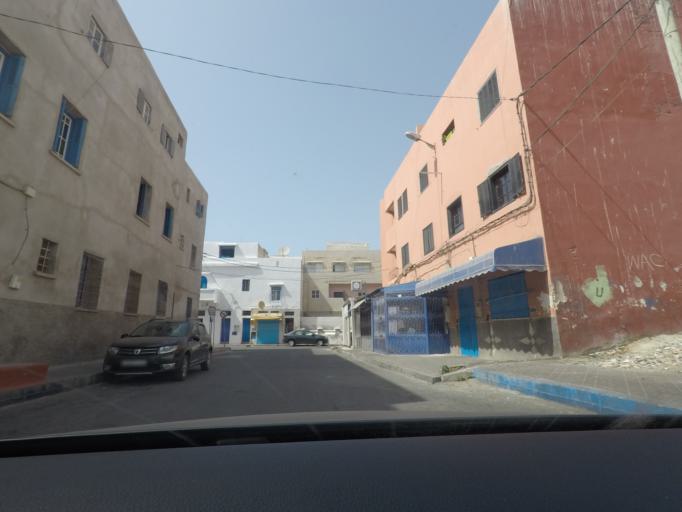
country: MA
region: Marrakech-Tensift-Al Haouz
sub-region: Essaouira
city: Essaouira
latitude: 31.5051
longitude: -9.7632
